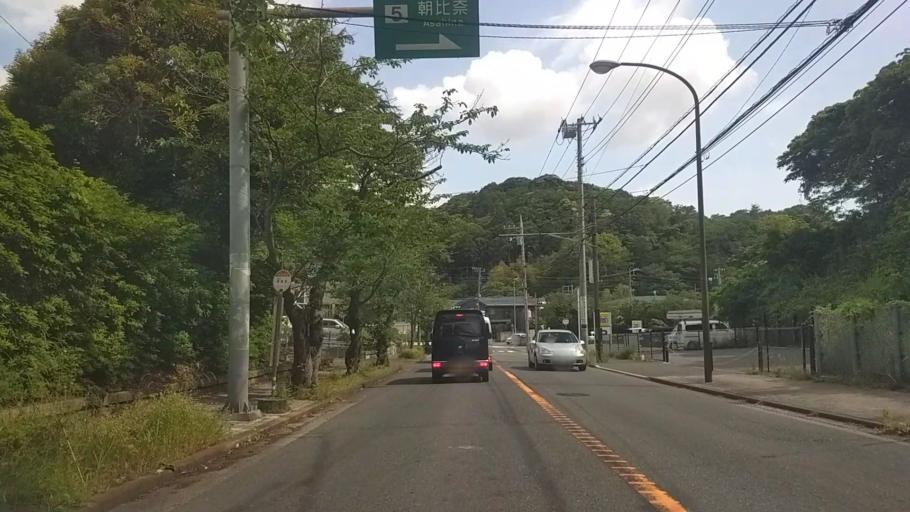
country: JP
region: Kanagawa
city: Zushi
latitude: 35.3185
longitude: 139.5772
